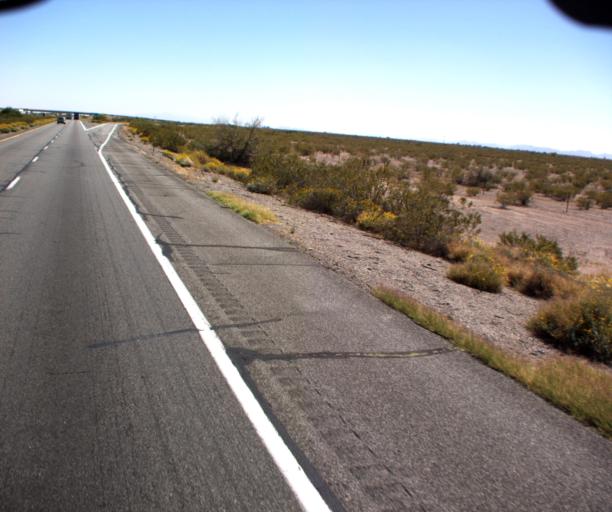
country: US
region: Arizona
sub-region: Maricopa County
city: Buckeye
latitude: 33.4836
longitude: -112.8759
